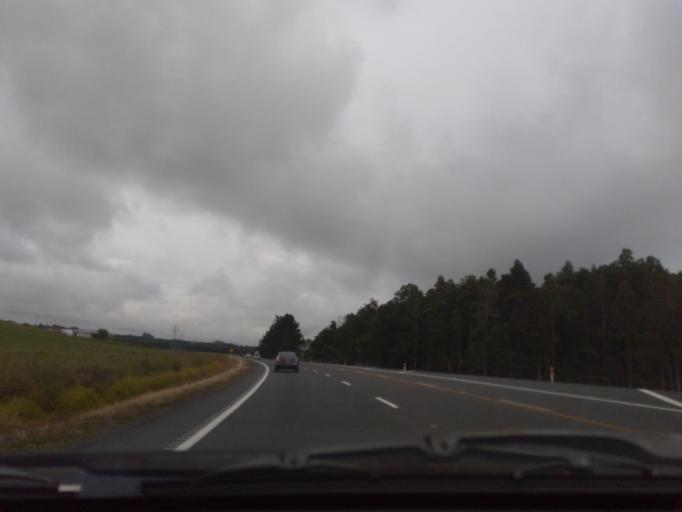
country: NZ
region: Northland
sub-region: Whangarei
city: Ruakaka
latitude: -35.8817
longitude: 174.4198
